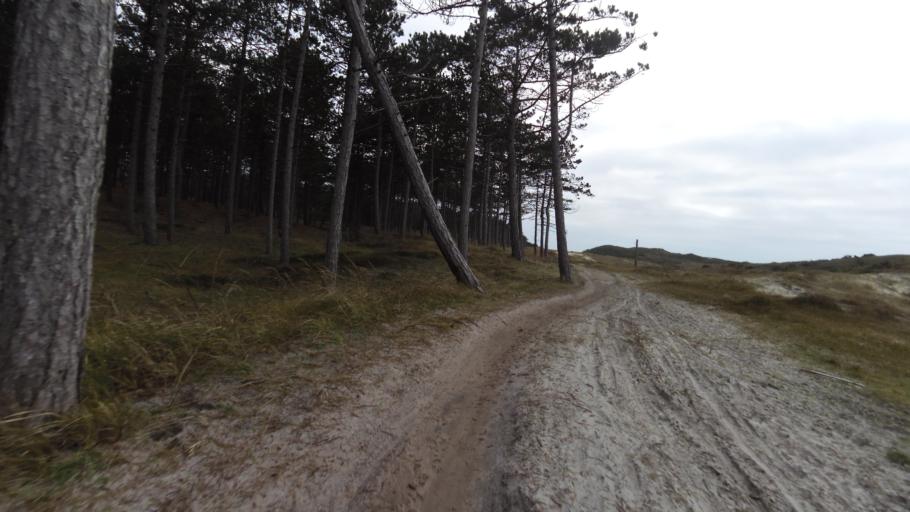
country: NL
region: North Holland
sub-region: Gemeente Bergen
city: Egmond aan Zee
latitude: 52.6900
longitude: 4.6437
